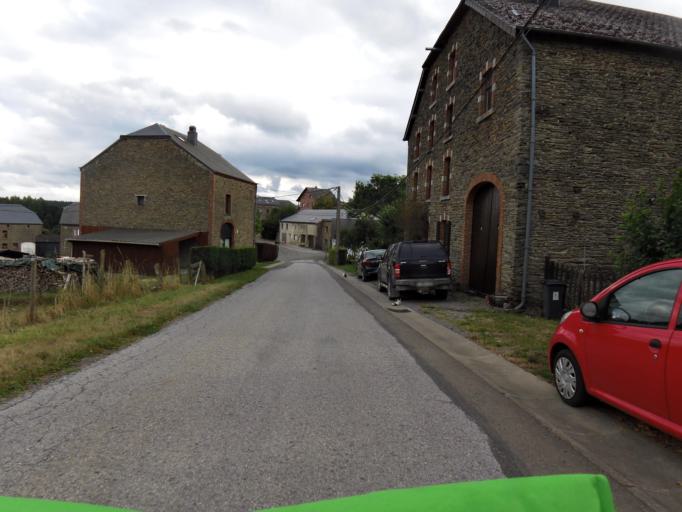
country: BE
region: Wallonia
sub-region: Province de Namur
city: Bievre
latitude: 49.9063
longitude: 4.9873
